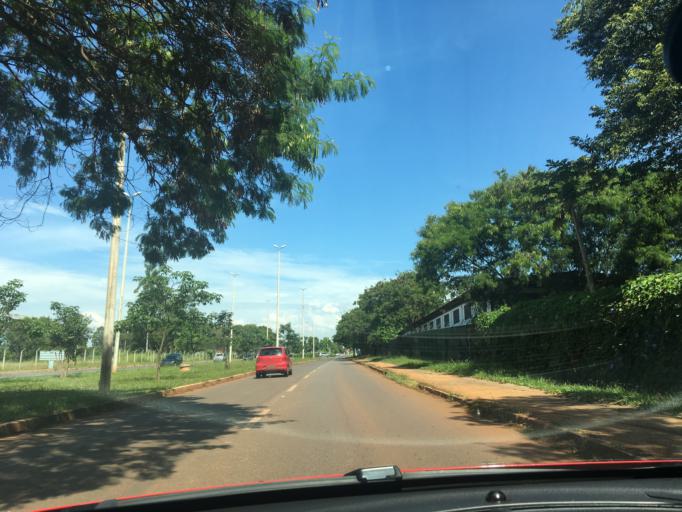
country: BR
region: Federal District
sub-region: Brasilia
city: Brasilia
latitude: -15.8058
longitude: -47.8654
